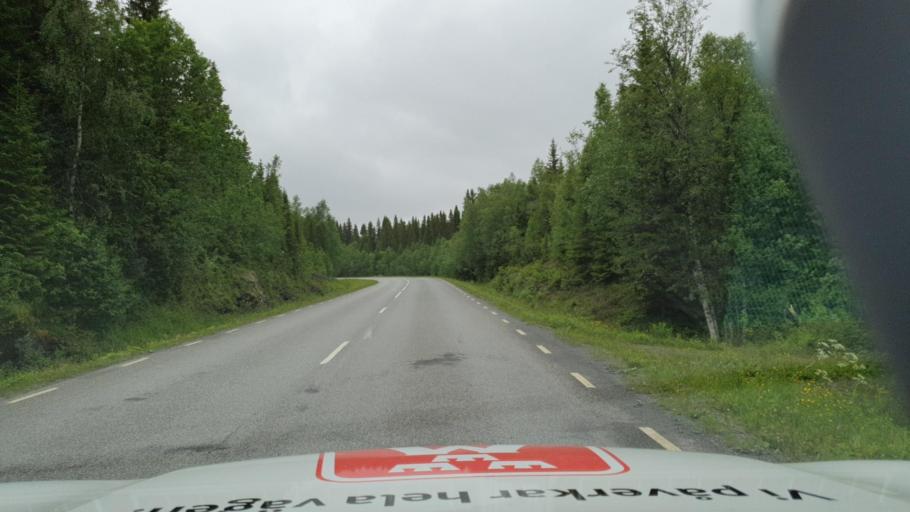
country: SE
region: Jaemtland
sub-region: Are Kommun
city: Are
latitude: 63.6768
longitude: 13.0509
